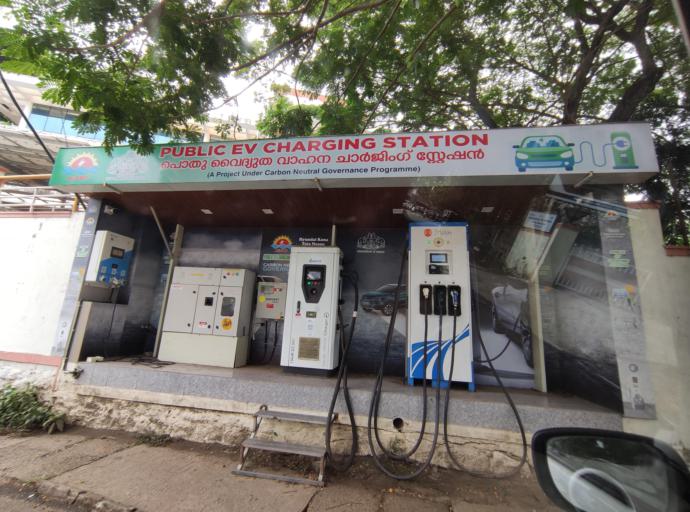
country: IN
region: Kerala
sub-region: Thiruvananthapuram
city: Thiruvananthapuram
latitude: 8.5086
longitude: 76.9462
